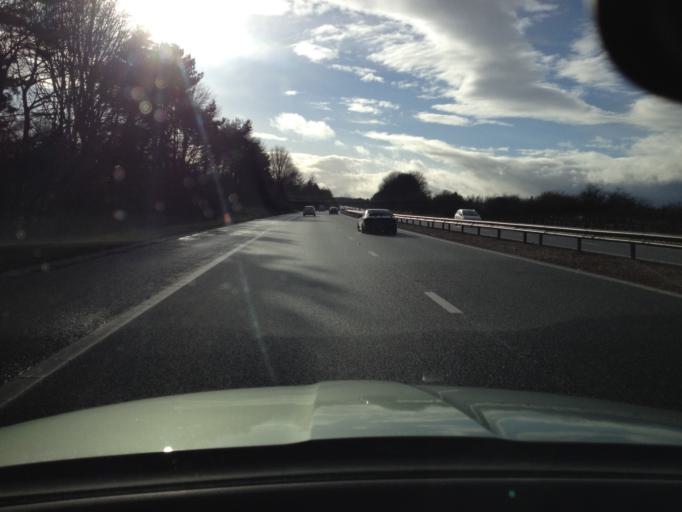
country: GB
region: Scotland
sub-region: West Lothian
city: Broxburn
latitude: 55.9204
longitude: -3.4789
